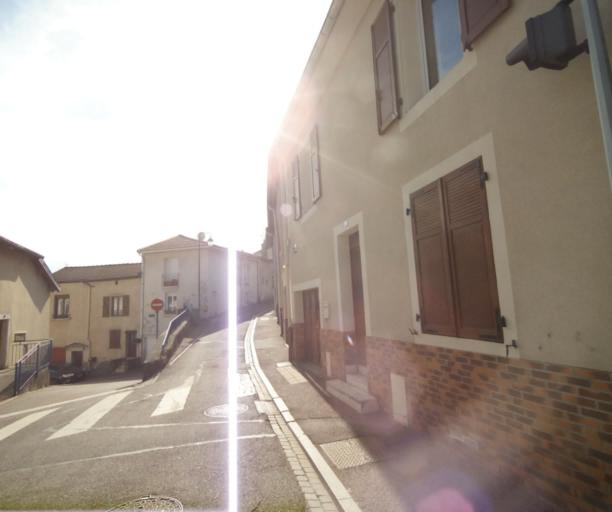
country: FR
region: Lorraine
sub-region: Departement de Meurthe-et-Moselle
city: Vandoeuvre-les-Nancy
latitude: 48.6569
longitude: 6.1662
